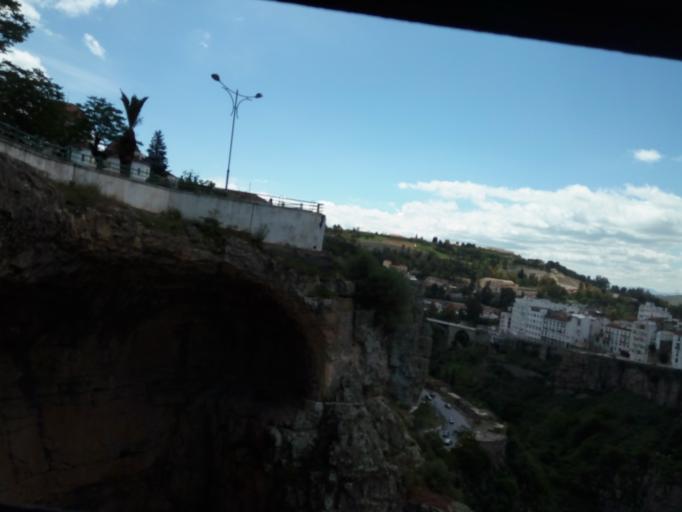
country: DZ
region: Constantine
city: Constantine
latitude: 36.3729
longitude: 6.6150
